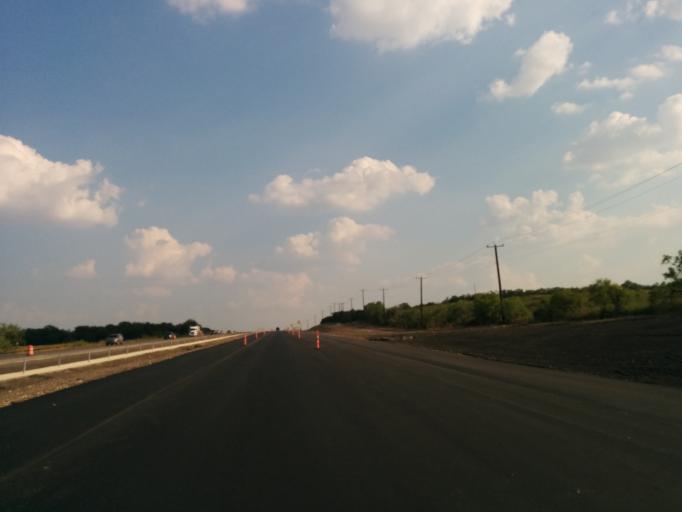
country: US
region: Texas
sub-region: Bexar County
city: Converse
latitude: 29.4750
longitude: -98.2952
